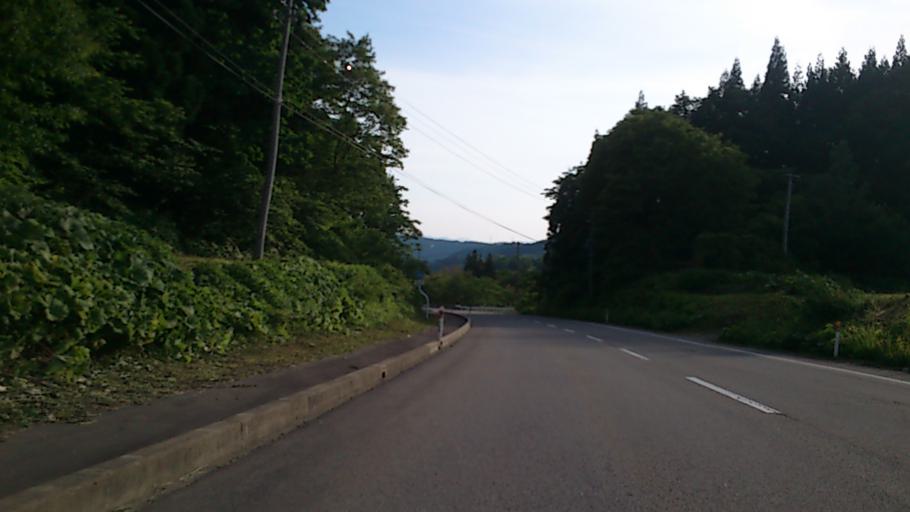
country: JP
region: Aomori
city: Kuroishi
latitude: 40.6266
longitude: 140.7049
